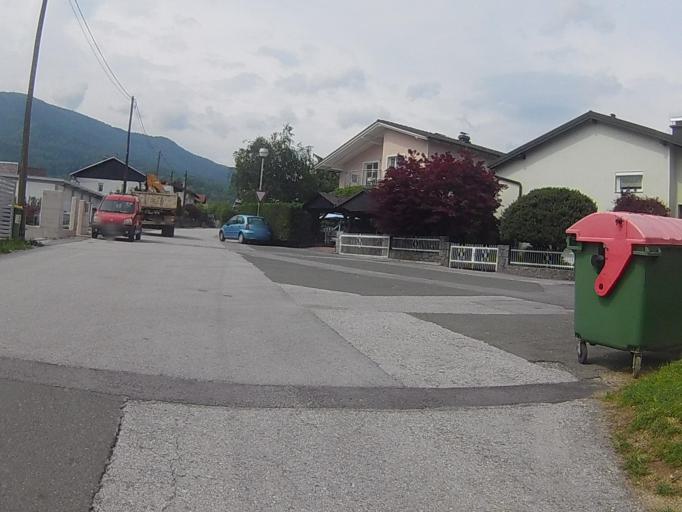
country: SI
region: Maribor
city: Pekre
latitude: 46.5430
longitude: 15.5923
